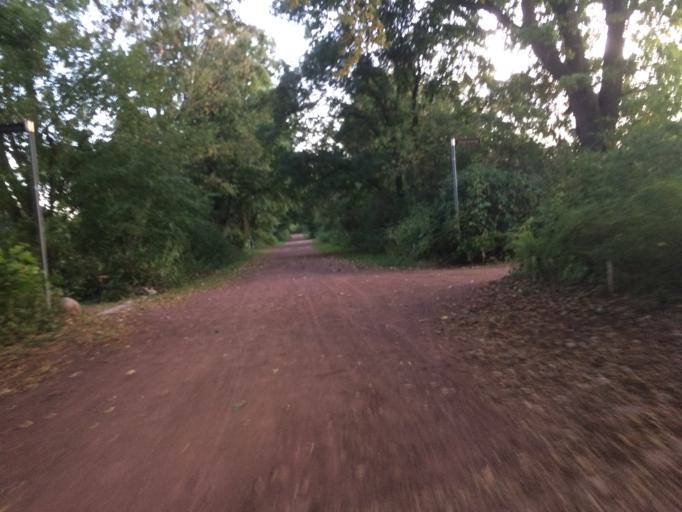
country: DE
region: Berlin
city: Stadtrandsiedlung Malchow
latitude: 52.5763
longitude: 13.4650
